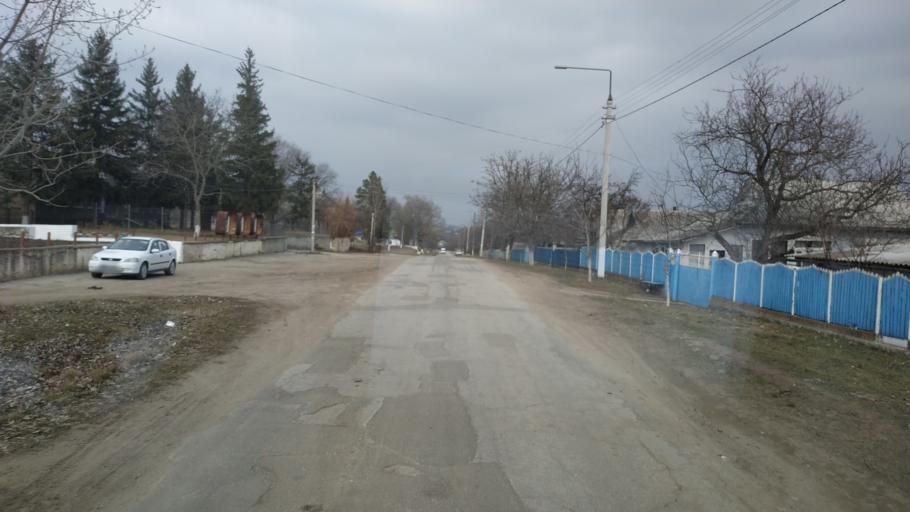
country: MD
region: Hincesti
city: Dancu
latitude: 46.8208
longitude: 28.2747
